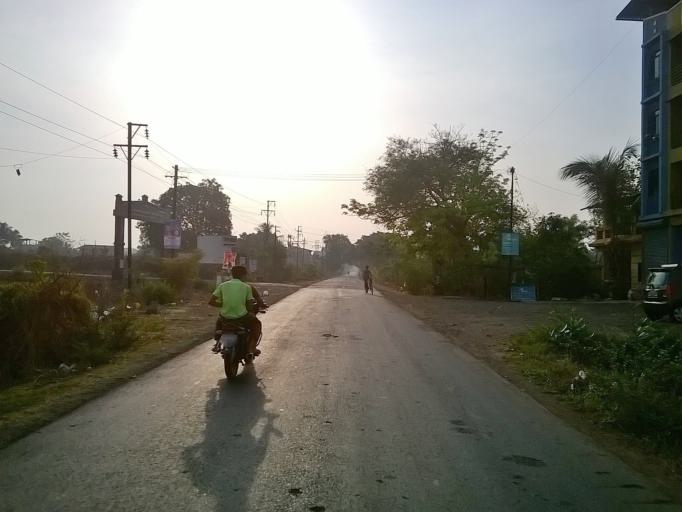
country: IN
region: Maharashtra
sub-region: Raigarh
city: Kalundri
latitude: 19.0131
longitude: 73.1648
